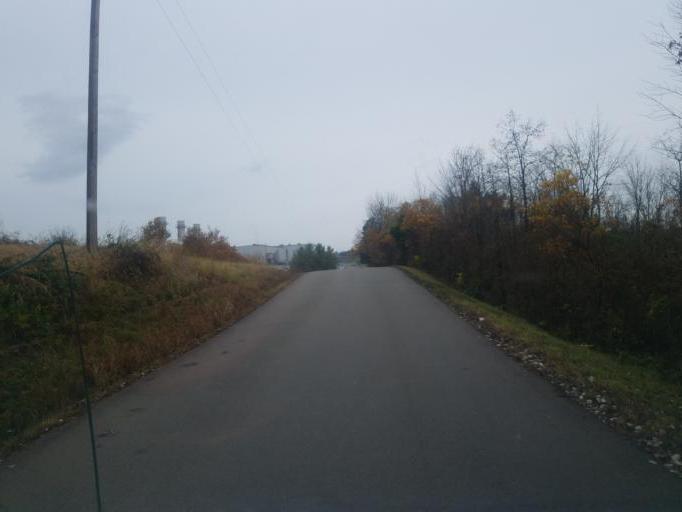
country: US
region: Ohio
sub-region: Washington County
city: Beverly
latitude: 39.5292
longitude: -81.7164
